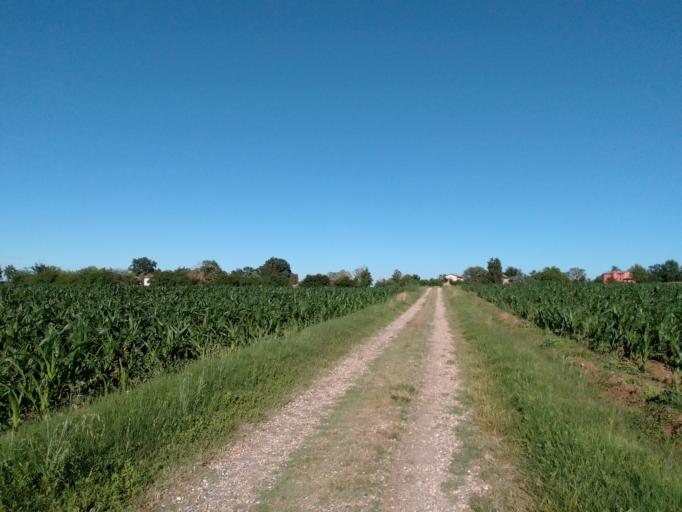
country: IT
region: Emilia-Romagna
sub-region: Provincia di Piacenza
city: Borgonovo Valtidone
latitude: 45.0068
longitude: 9.4273
